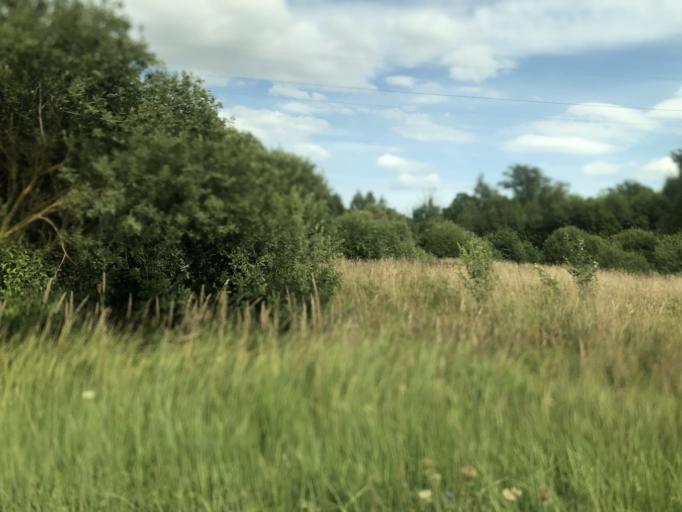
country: LV
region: Vecumnieki
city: Vecumnieki
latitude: 56.4580
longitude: 24.6327
